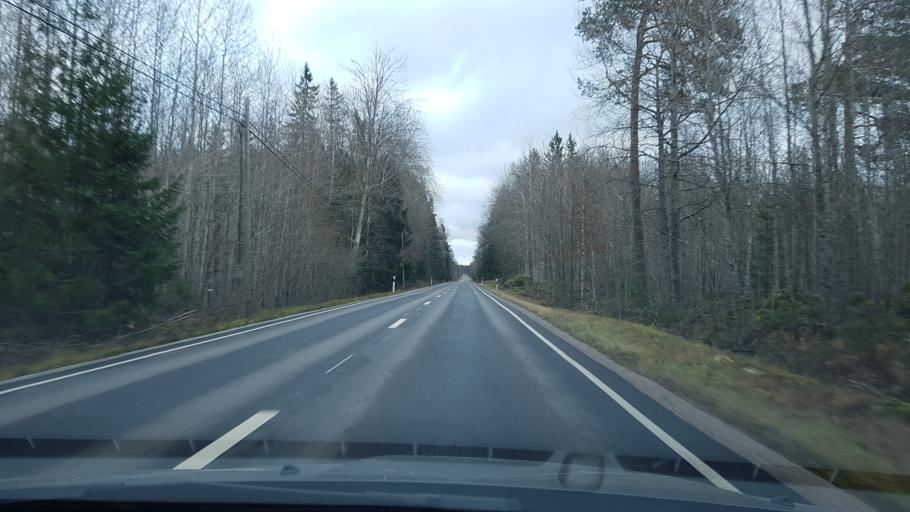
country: SE
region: Stockholm
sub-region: Norrtalje Kommun
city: Skanninge
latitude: 60.0178
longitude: 18.3604
